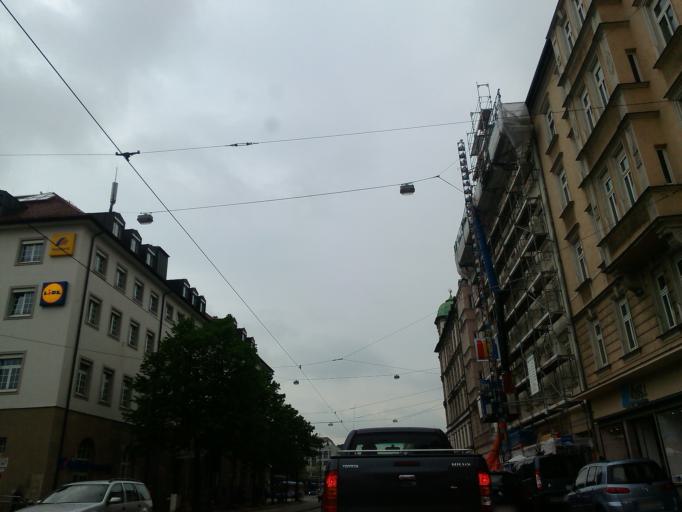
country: DE
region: Bavaria
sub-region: Upper Bavaria
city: Bogenhausen
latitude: 48.1293
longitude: 11.6053
